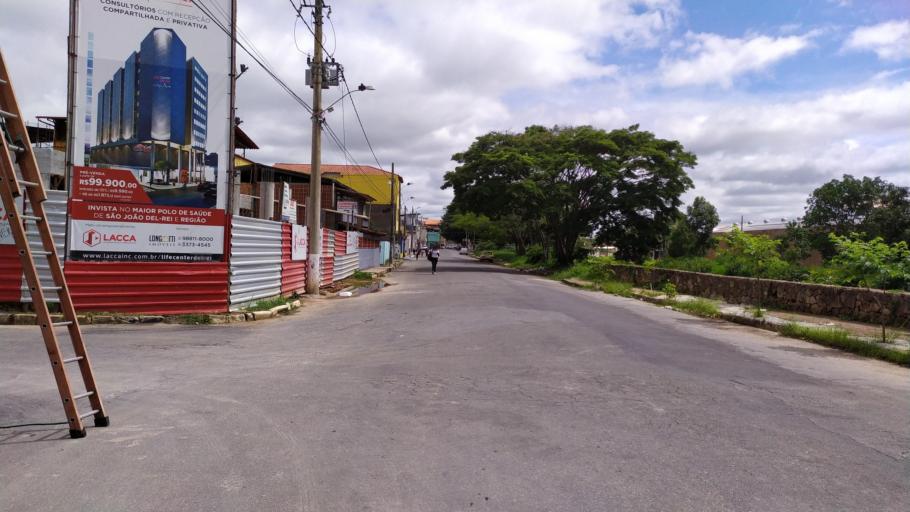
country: BR
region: Minas Gerais
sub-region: Sao Joao Del Rei
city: Sao Joao del Rei
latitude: -21.1239
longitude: -44.2454
